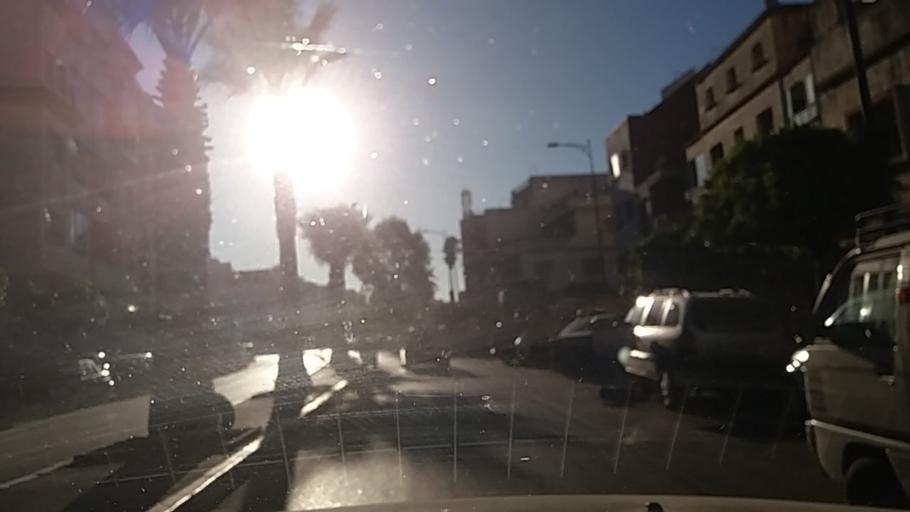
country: MA
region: Tanger-Tetouan
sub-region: Tanger-Assilah
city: Tangier
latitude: 35.7696
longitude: -5.8193
